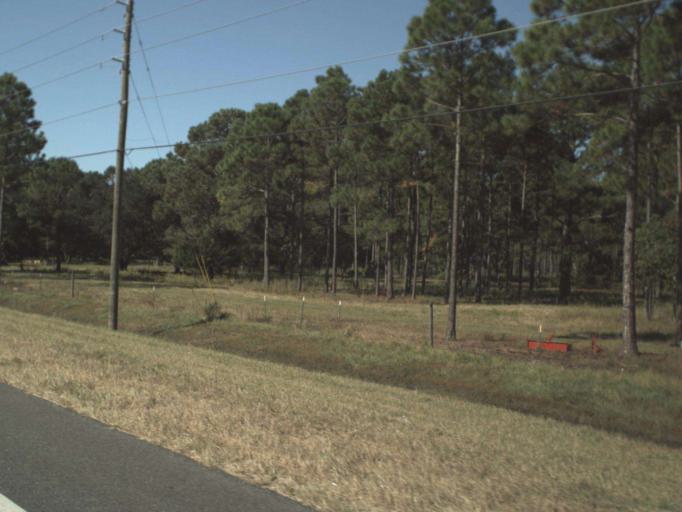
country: US
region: Florida
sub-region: Walton County
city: Freeport
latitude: 30.4392
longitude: -86.1489
